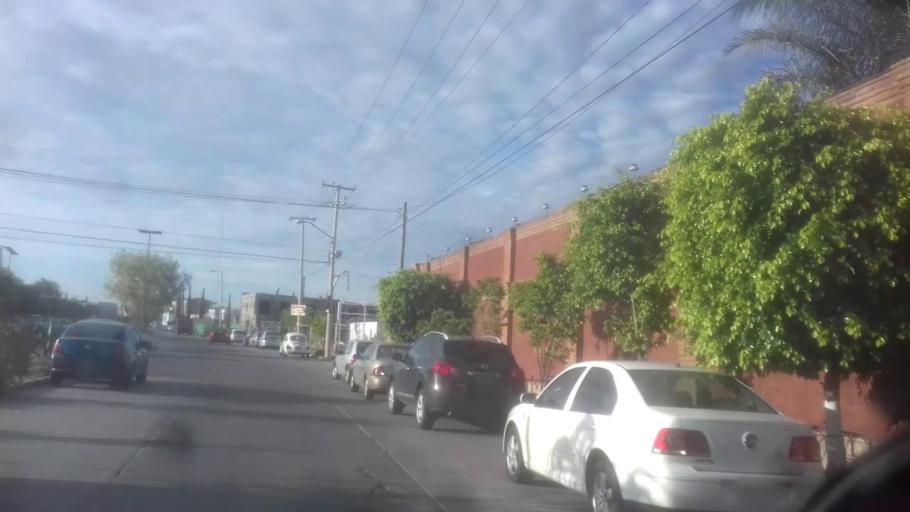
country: MX
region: Aguascalientes
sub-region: Aguascalientes
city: Aguascalientes
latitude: 21.8576
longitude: -102.2864
